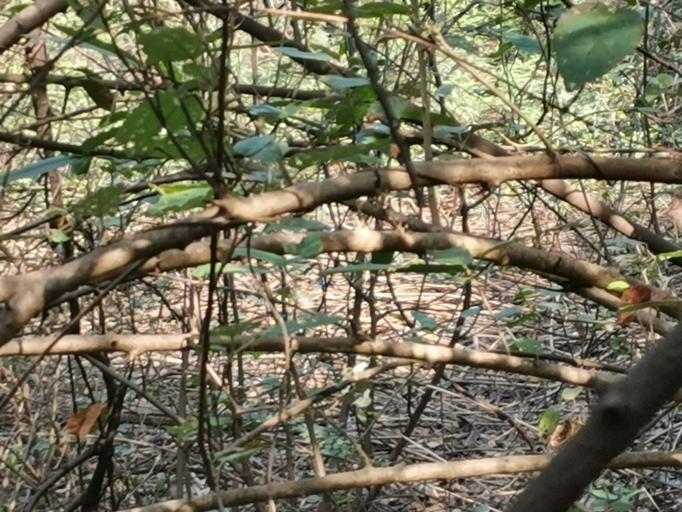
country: KH
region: Battambang
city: Battambang
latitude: 13.2998
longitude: 103.3867
